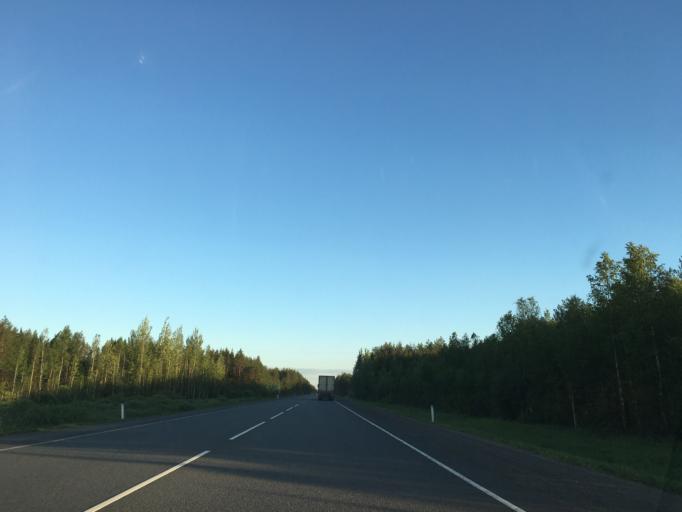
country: RU
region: Leningrad
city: Rozhdestveno
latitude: 59.2994
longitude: 29.9413
